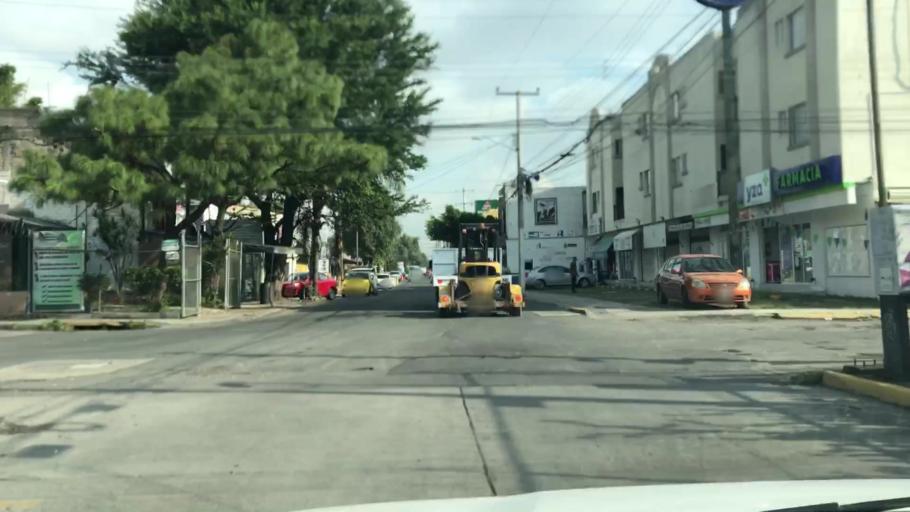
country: MX
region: Jalisco
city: Guadalajara
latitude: 20.6437
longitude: -103.4328
